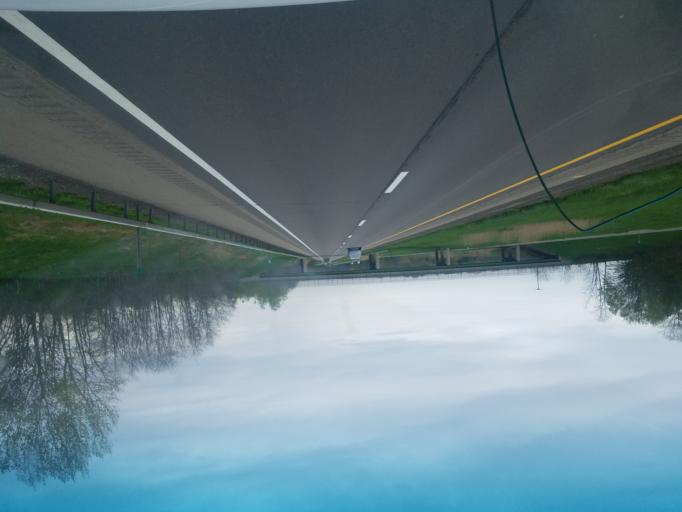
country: US
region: New York
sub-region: Chautauqua County
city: Brocton
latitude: 42.3908
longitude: -79.4742
